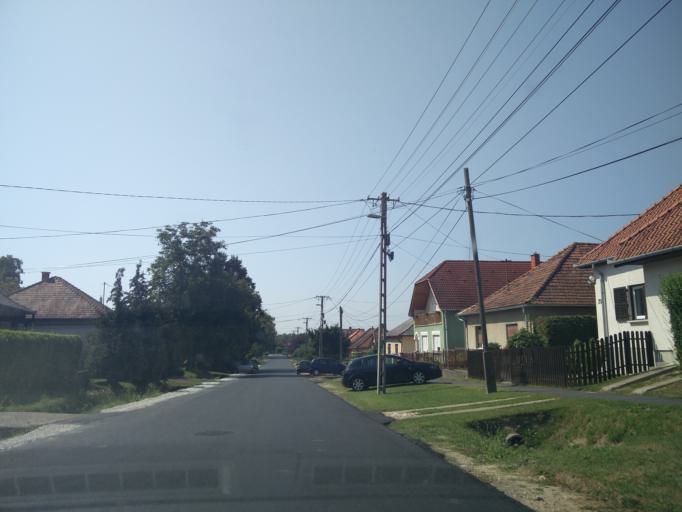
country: HU
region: Zala
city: Zalaegerszeg
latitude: 46.8444
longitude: 16.8773
